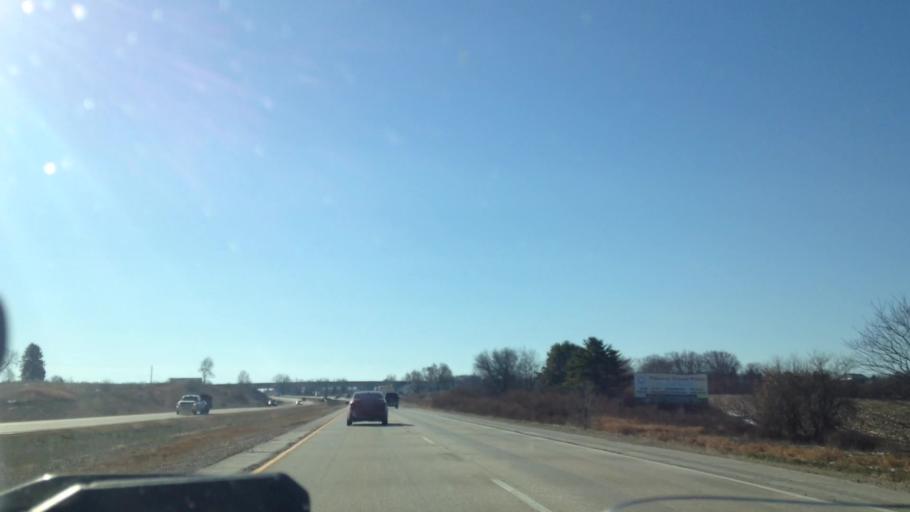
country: US
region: Wisconsin
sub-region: Washington County
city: Jackson
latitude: 43.2995
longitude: -88.1870
